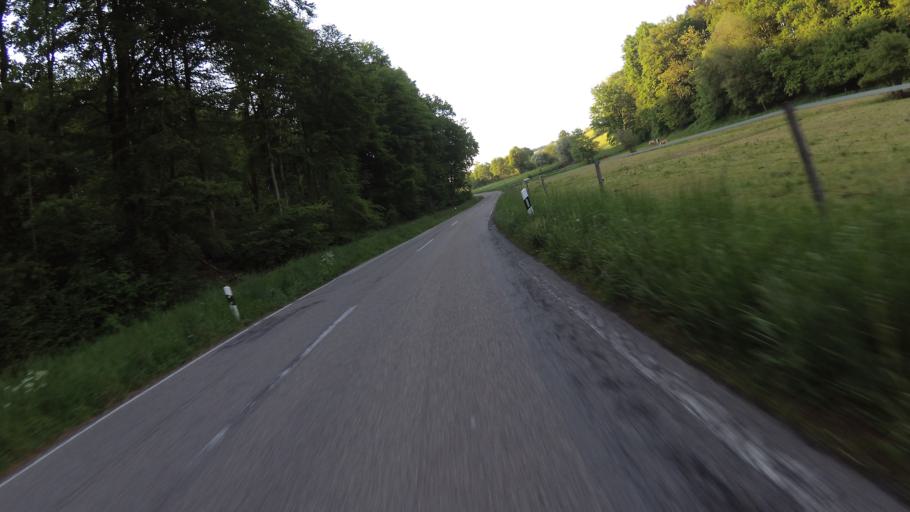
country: DE
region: Rheinland-Pfalz
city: Contwig
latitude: 49.2181
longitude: 7.4192
